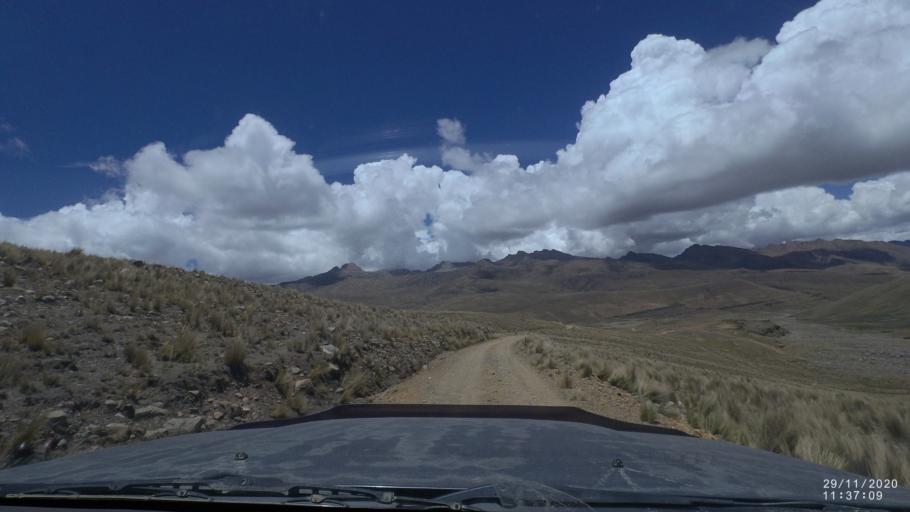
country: BO
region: Cochabamba
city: Cochabamba
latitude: -17.1968
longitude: -66.2309
